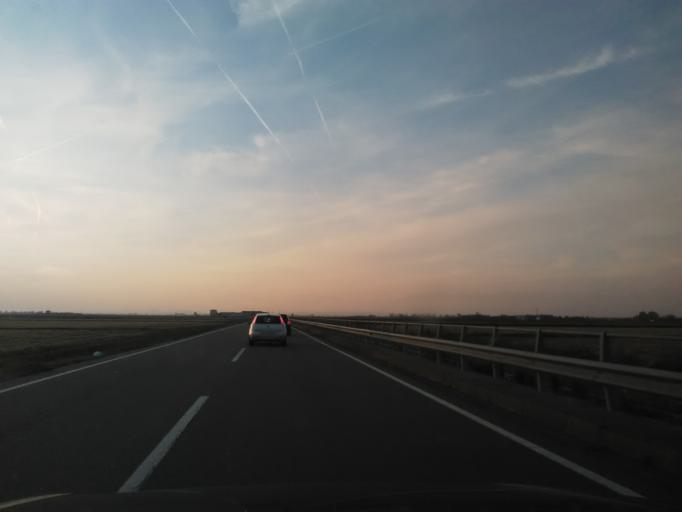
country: IT
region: Piedmont
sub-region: Provincia di Vercelli
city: Olcenengo
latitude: 45.3362
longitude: 8.3020
